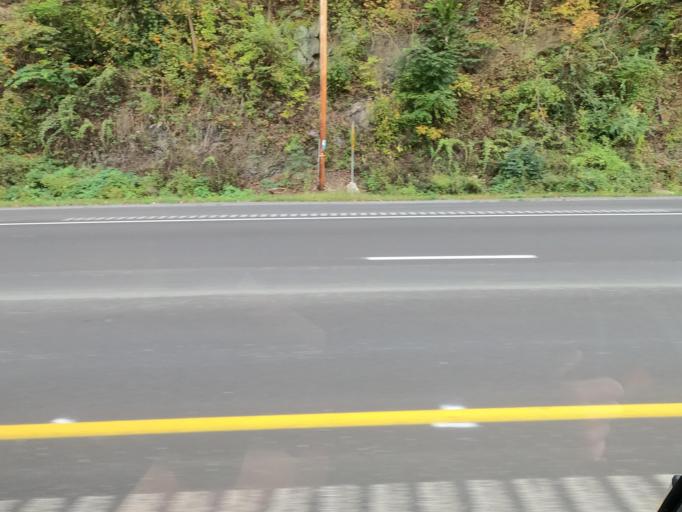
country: US
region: Tennessee
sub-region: Sullivan County
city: Colonial Heights
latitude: 36.5100
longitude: -82.5393
